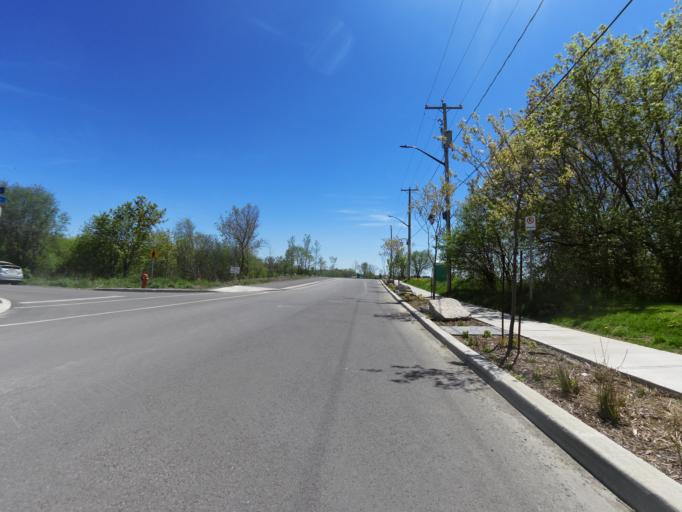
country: CA
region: Ontario
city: Bells Corners
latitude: 45.3808
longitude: -75.8046
